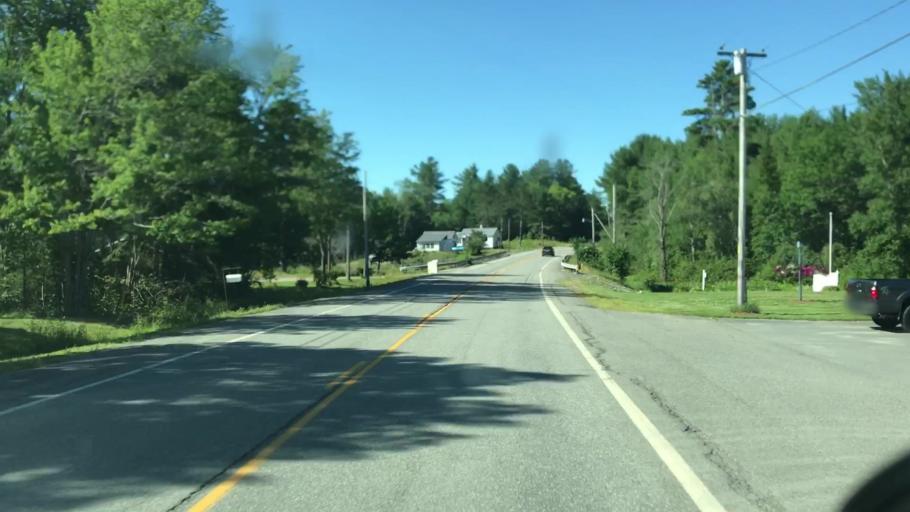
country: US
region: Maine
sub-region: Penobscot County
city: Howland
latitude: 45.2880
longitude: -68.6241
